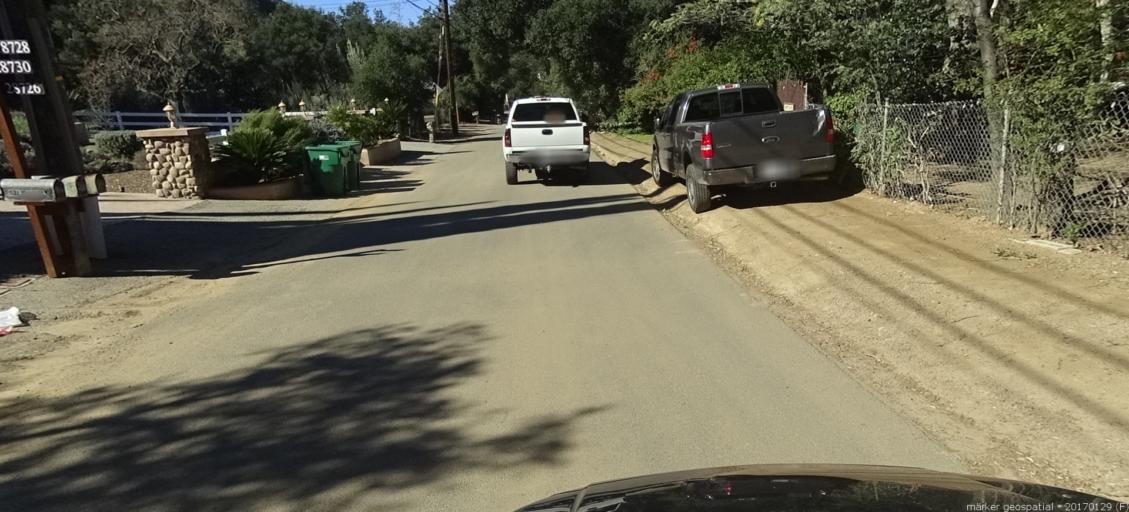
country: US
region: California
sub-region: Orange County
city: Portola Hills
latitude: 33.7080
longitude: -117.6295
